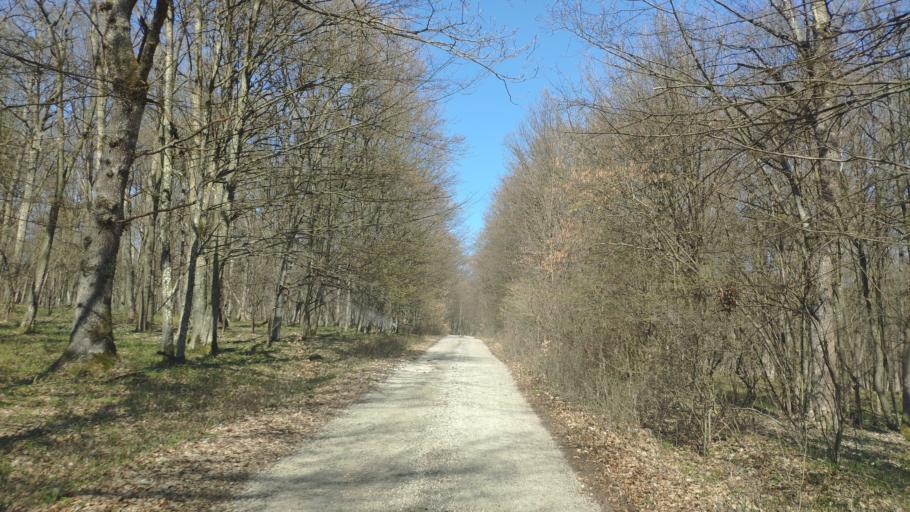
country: SK
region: Kosicky
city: Roznava
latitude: 48.5883
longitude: 20.4093
